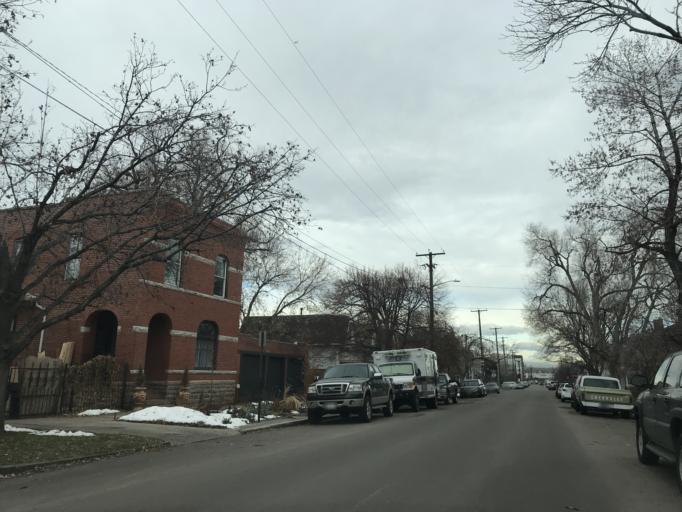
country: US
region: Colorado
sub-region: Denver County
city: Denver
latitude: 39.7595
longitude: -104.9792
